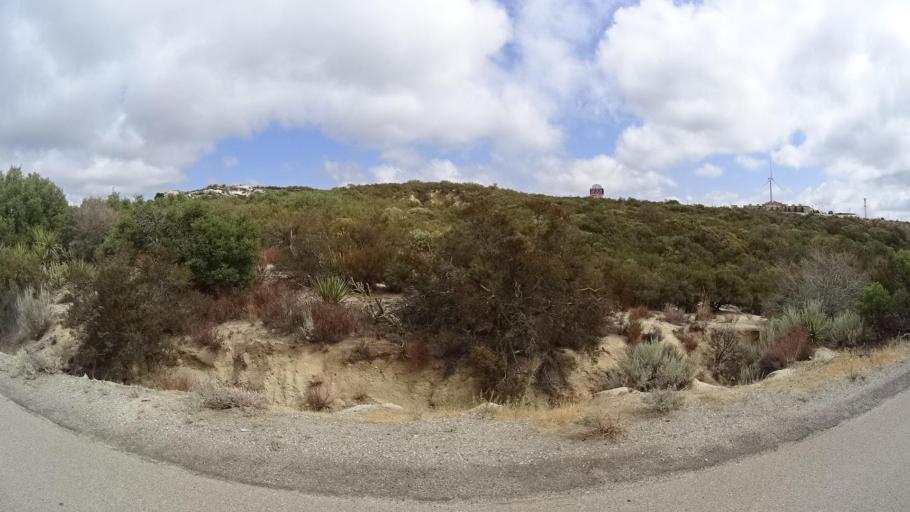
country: US
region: California
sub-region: San Diego County
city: Campo
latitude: 32.7034
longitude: -116.3597
